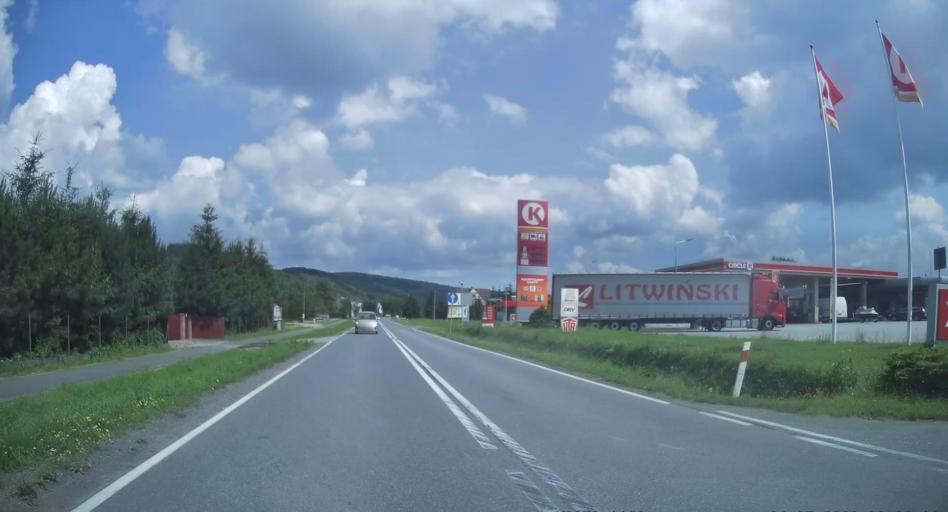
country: PL
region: Lesser Poland Voivodeship
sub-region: Powiat tarnowski
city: Wielka Wies
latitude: 49.8992
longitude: 20.8155
